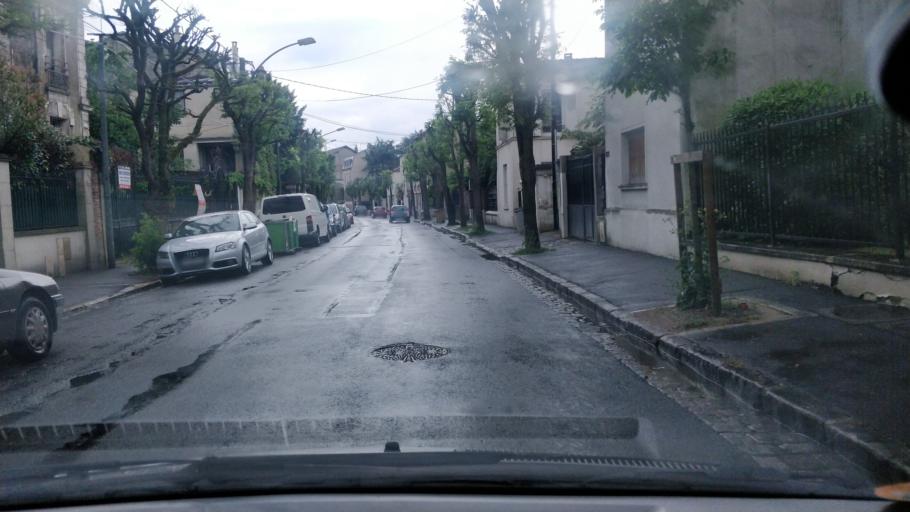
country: FR
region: Ile-de-France
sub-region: Departement de Seine-Saint-Denis
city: Le Raincy
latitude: 48.8951
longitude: 2.5090
